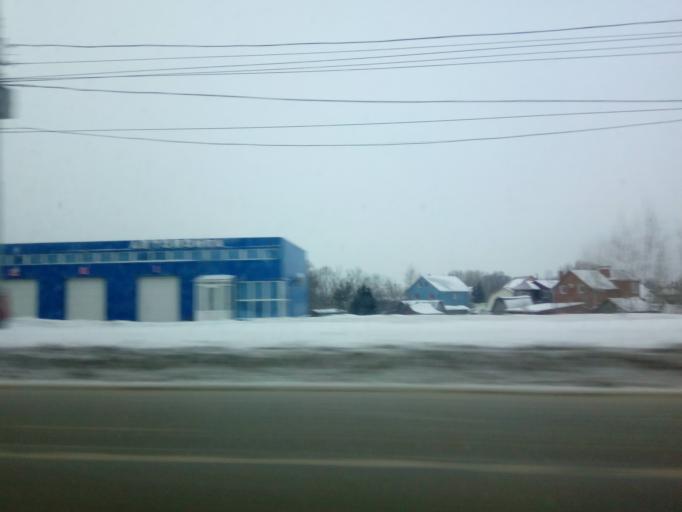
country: RU
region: Novosibirsk
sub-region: Novosibirskiy Rayon
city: Novosibirsk
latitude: 55.0120
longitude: 82.8781
